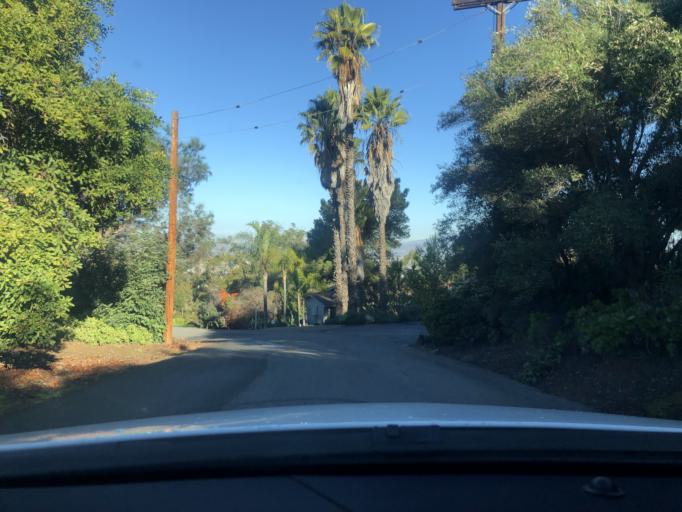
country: US
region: California
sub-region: San Diego County
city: Casa de Oro-Mount Helix
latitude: 32.7736
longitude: -116.9604
